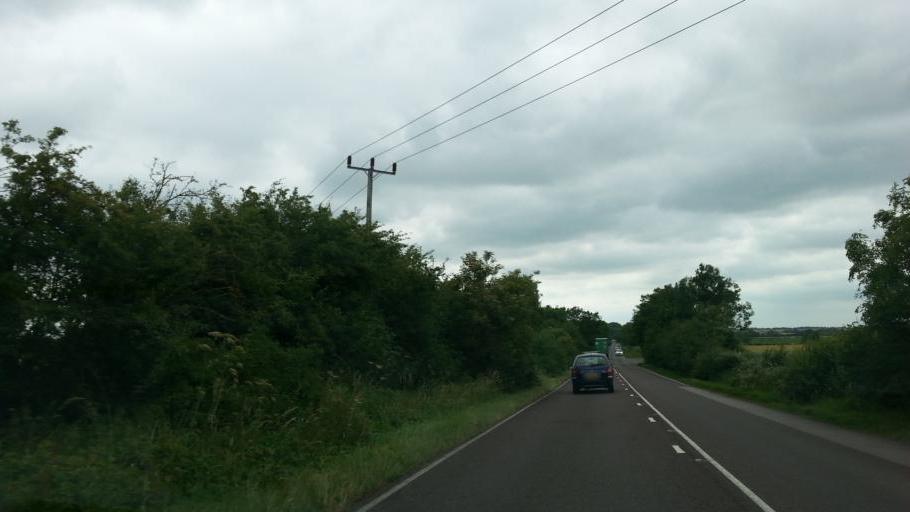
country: GB
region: England
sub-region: Cambridgeshire
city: Papworth Everard
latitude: 52.2656
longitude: -0.1299
